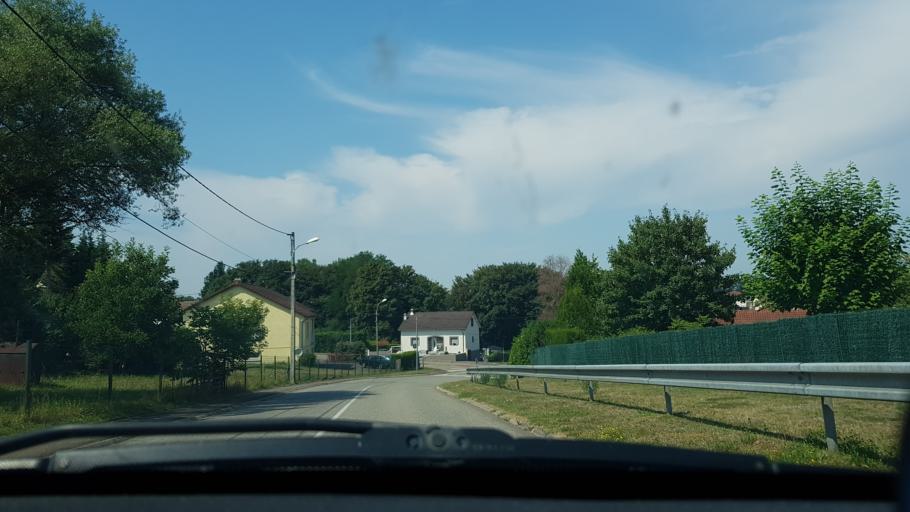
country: FR
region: Lorraine
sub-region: Departement de la Moselle
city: Diesen
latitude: 49.1766
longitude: 6.6809
